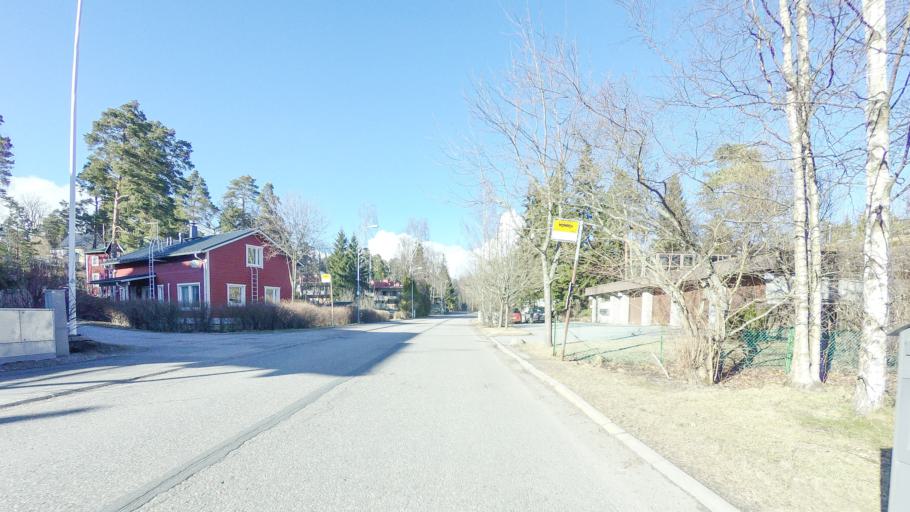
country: FI
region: Uusimaa
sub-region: Helsinki
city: Helsinki
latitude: 60.1749
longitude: 25.0242
